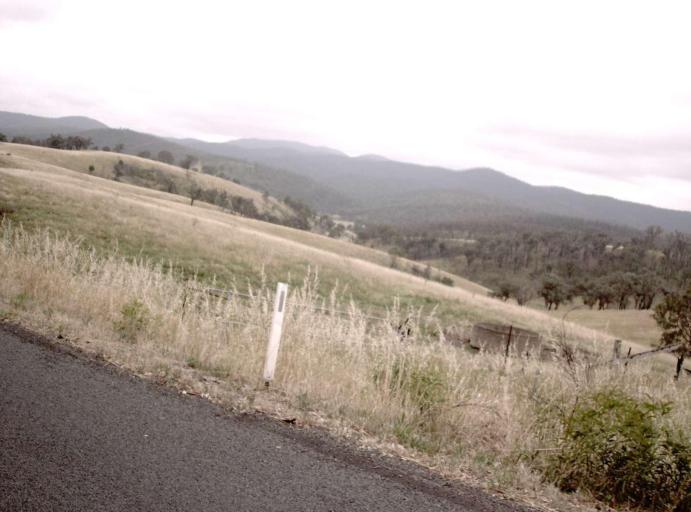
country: AU
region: Victoria
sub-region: Wellington
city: Heyfield
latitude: -37.8629
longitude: 146.7075
